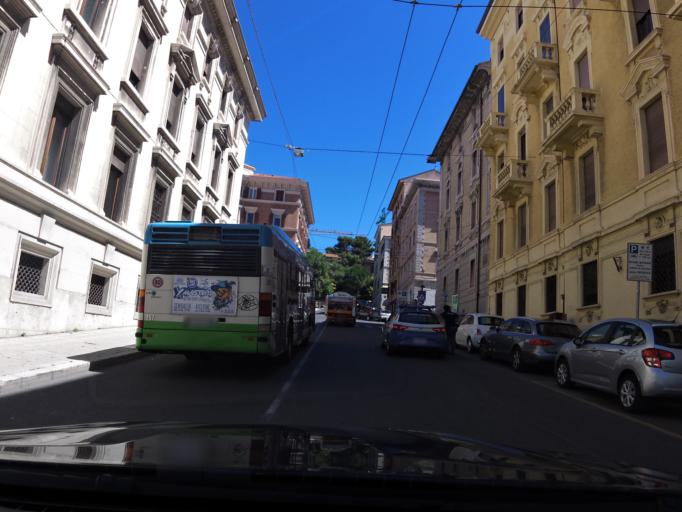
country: IT
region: The Marches
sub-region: Provincia di Ancona
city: Le Grazie di Ancona
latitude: 43.6164
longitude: 13.5192
